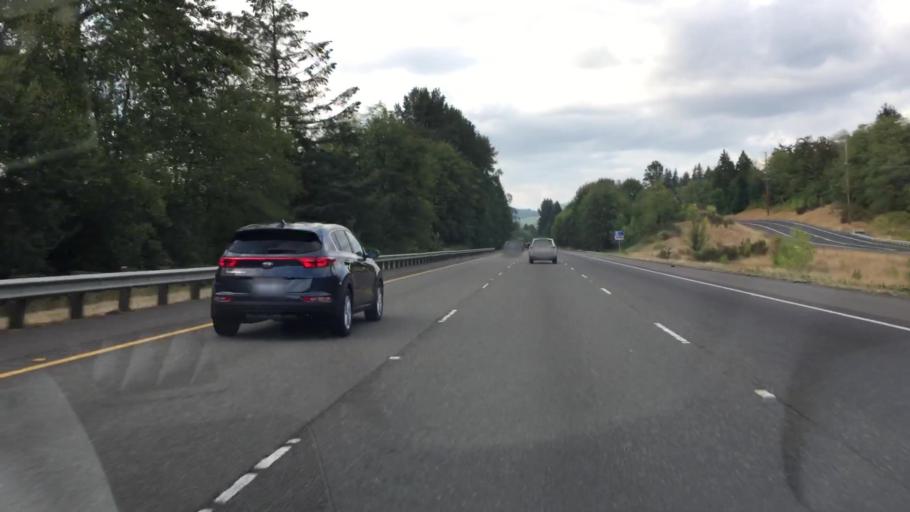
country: US
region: Washington
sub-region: Cowlitz County
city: West Side Highway
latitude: 46.2183
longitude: -122.8911
